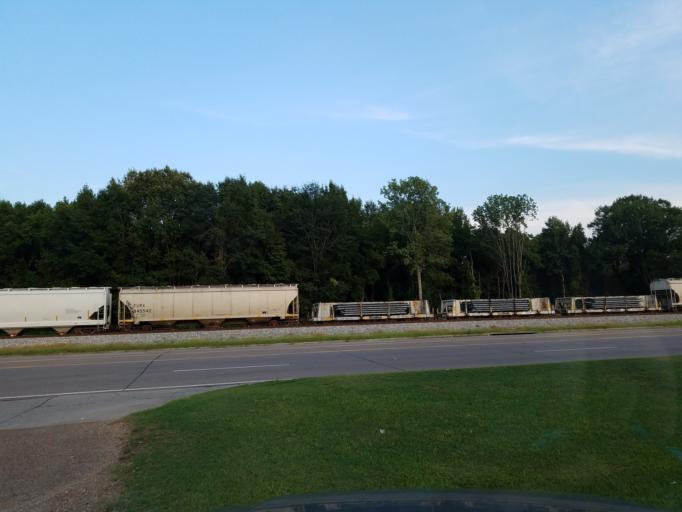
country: US
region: Mississippi
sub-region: Lauderdale County
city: Meridian
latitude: 32.3509
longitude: -88.7372
